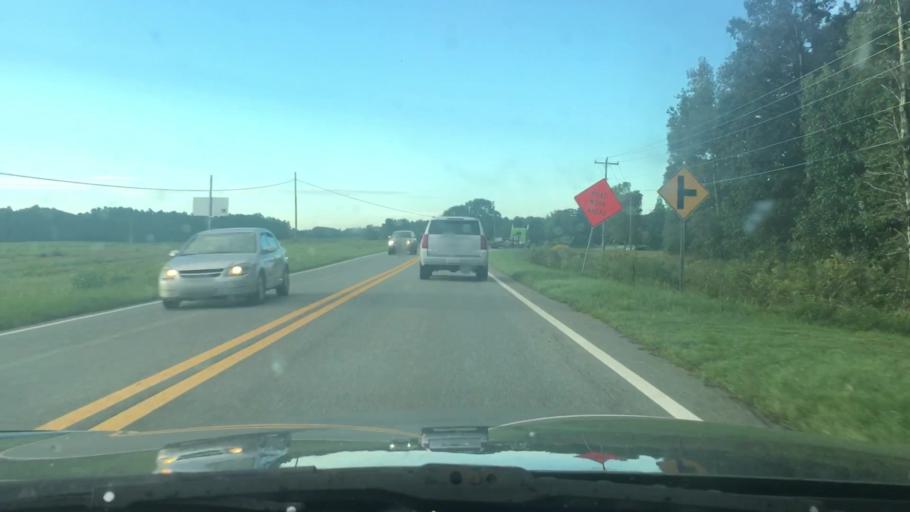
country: US
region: North Carolina
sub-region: Alamance County
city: Green Level
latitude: 36.1808
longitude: -79.3284
